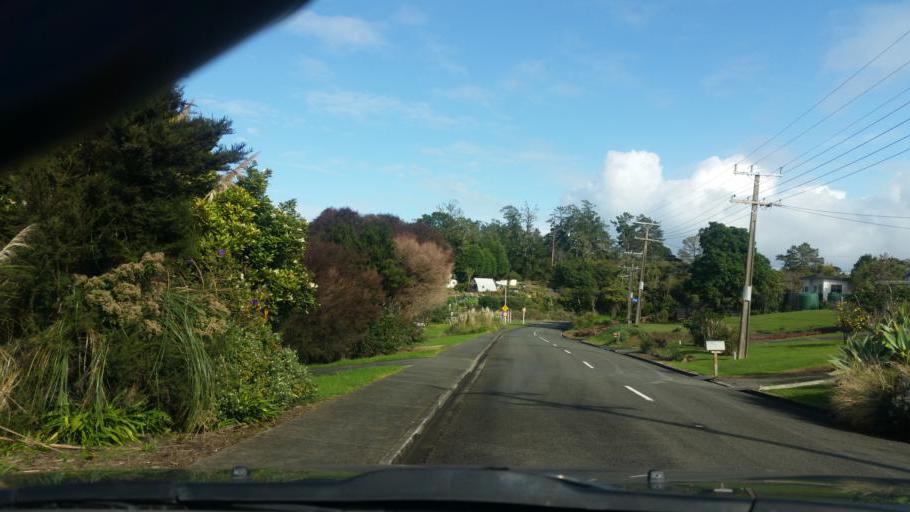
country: NZ
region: Auckland
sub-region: Auckland
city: Wellsford
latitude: -36.2471
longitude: 174.2479
